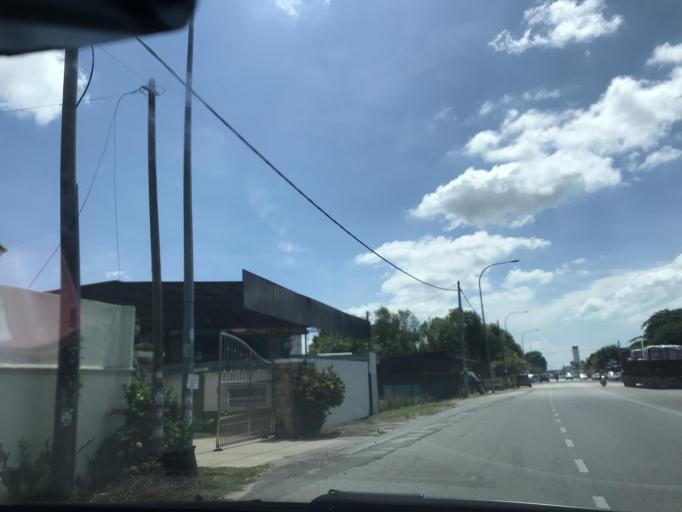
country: MY
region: Kelantan
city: Kota Bharu
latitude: 6.1118
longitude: 102.2641
